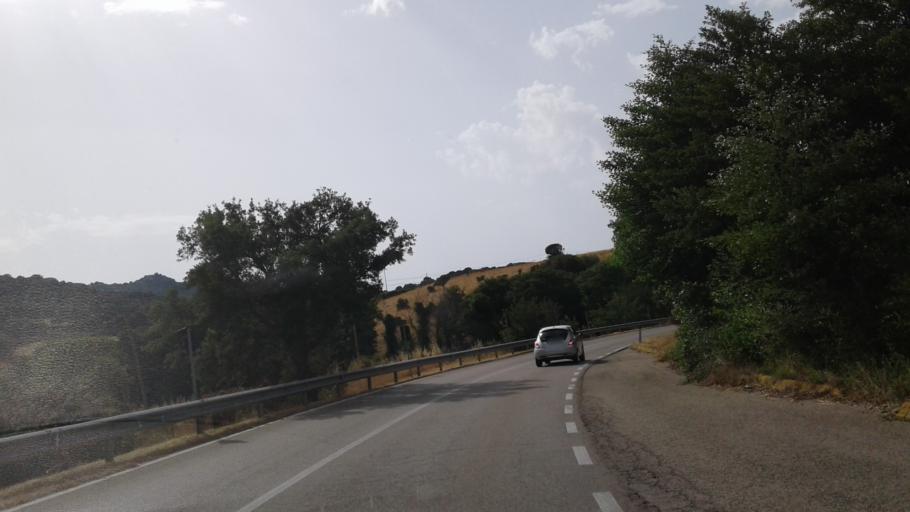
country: IT
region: Sardinia
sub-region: Provincia di Olbia-Tempio
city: Sant'Antonio di Gallura
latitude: 40.9646
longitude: 9.2790
